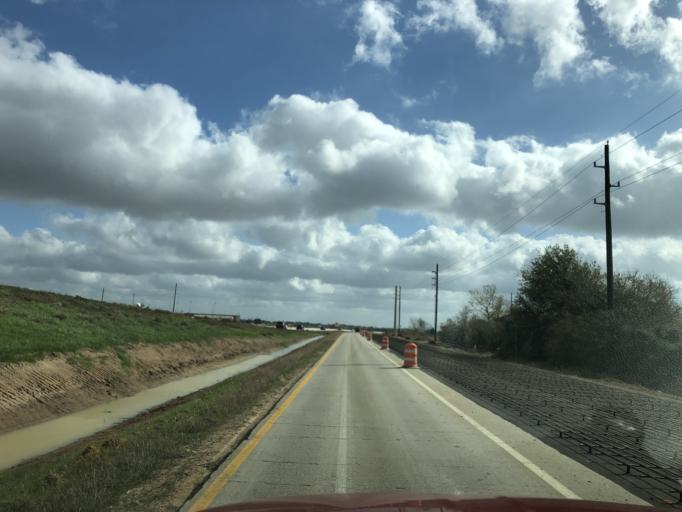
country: US
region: Texas
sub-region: Austin County
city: Sealy
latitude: 29.7619
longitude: -96.1828
